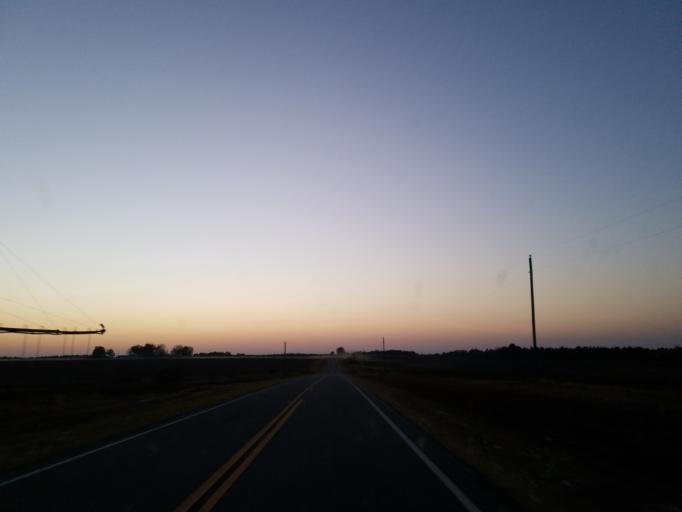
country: US
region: Georgia
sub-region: Wilcox County
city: Rochelle
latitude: 31.8536
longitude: -83.5797
